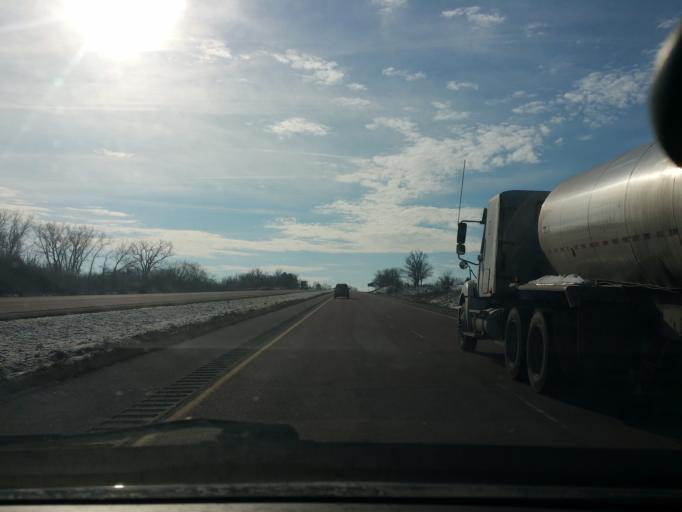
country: US
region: Iowa
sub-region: Warren County
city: Norwalk
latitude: 41.3190
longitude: -93.7796
